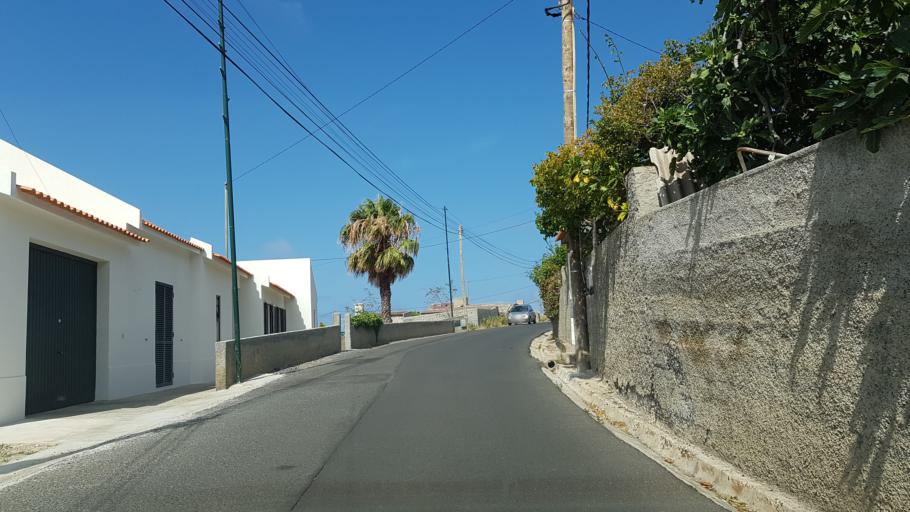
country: PT
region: Madeira
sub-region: Porto Santo
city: Vila de Porto Santo
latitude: 33.0711
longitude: -16.3300
